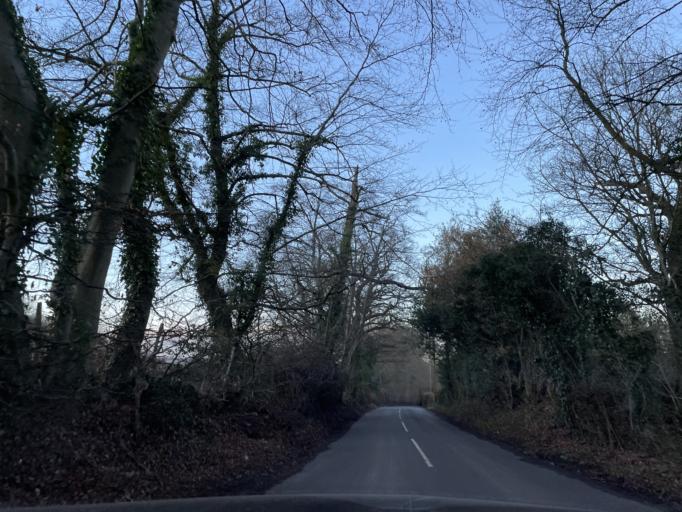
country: GB
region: England
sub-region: Kent
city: Westerham
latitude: 51.2669
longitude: 0.1258
